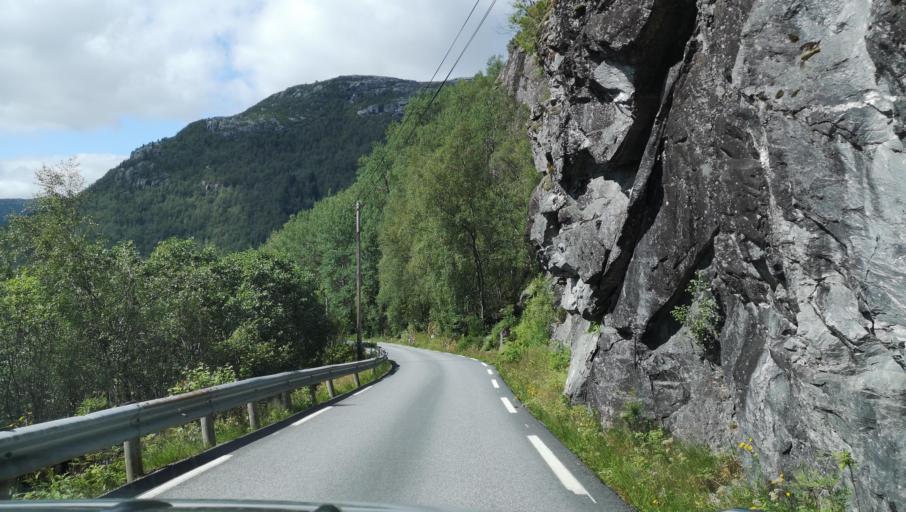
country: NO
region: Hordaland
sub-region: Modalen
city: Mo
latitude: 60.7820
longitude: 5.9461
